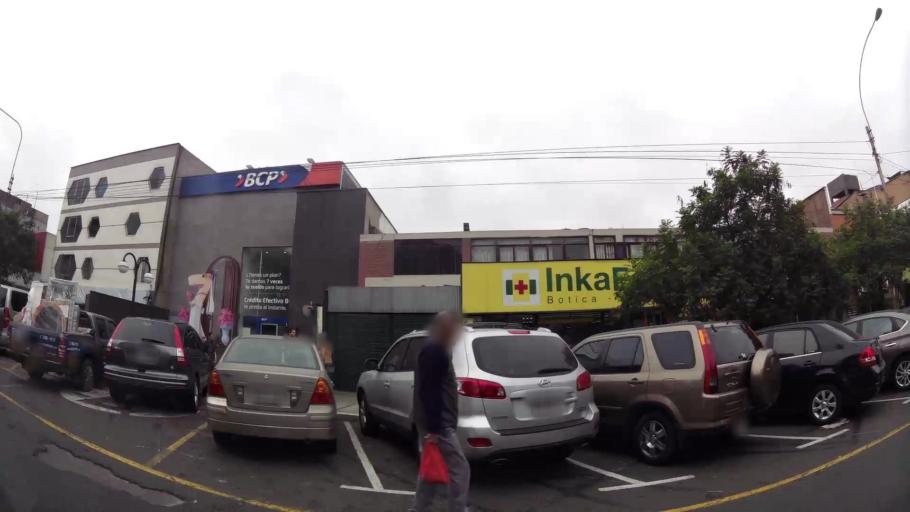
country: PE
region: Lima
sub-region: Lima
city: San Luis
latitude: -12.0892
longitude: -76.9962
